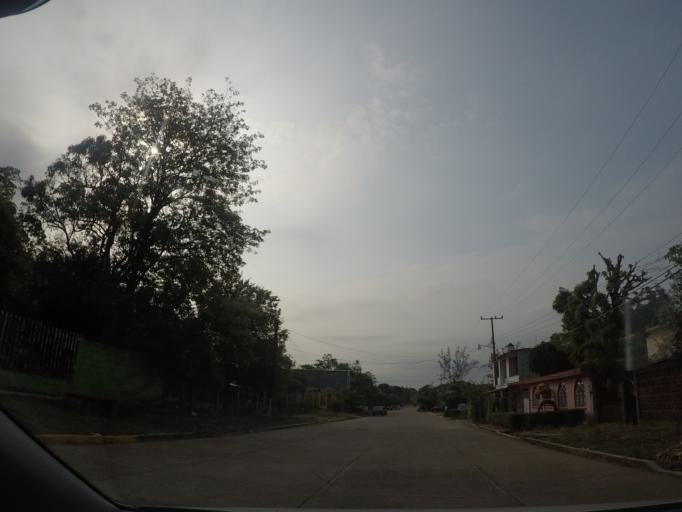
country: MX
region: Oaxaca
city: Colonia Rincon Viejo
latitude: 16.8845
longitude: -95.0428
